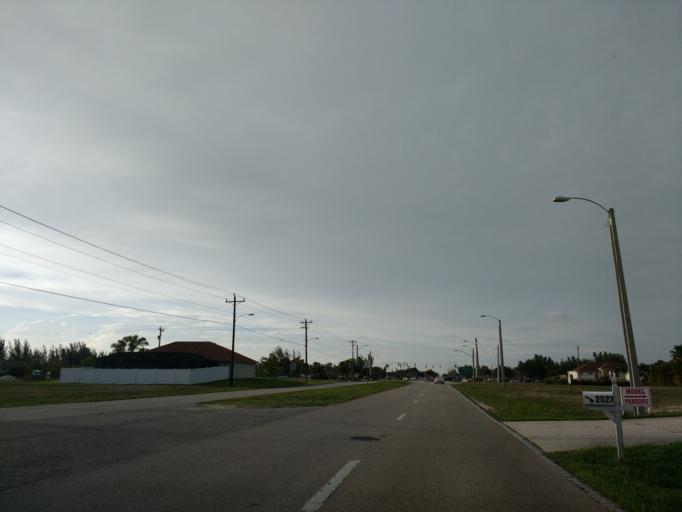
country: US
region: Florida
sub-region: Lee County
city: Cape Coral
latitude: 26.6048
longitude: -82.0070
